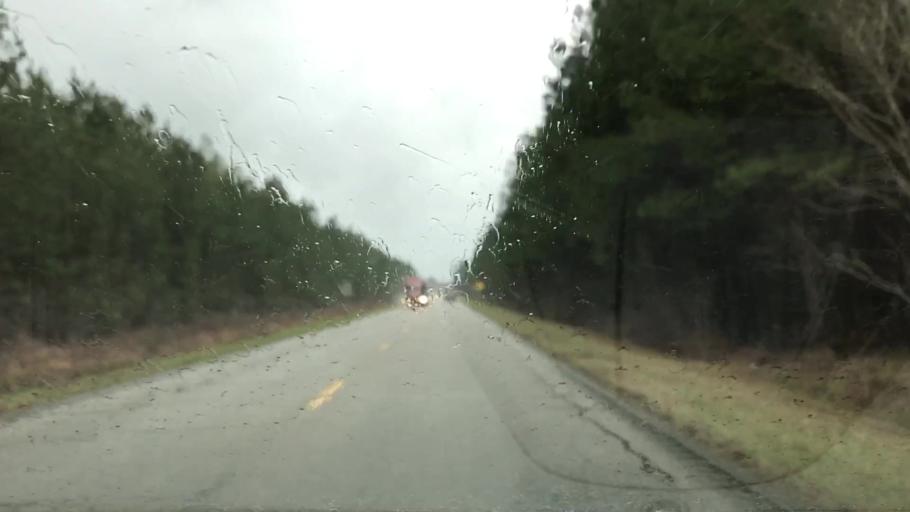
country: US
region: South Carolina
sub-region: Williamsburg County
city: Andrews
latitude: 33.5434
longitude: -79.4753
